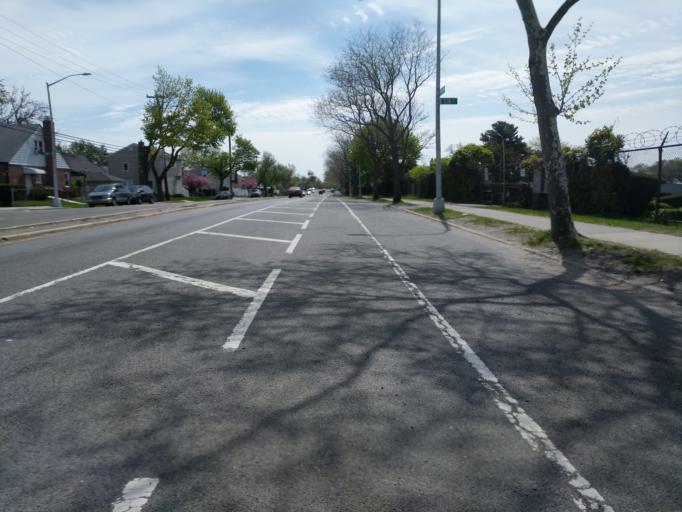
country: US
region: New York
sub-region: Nassau County
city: Elmont
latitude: 40.6865
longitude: -73.7369
